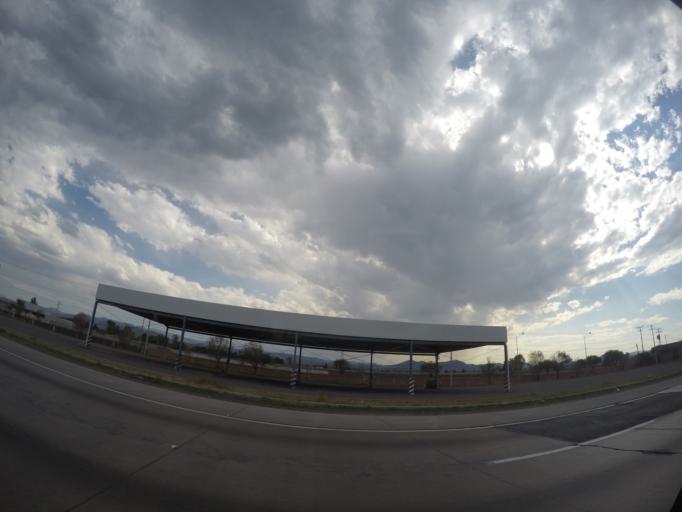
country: MX
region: Queretaro
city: La Estancia
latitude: 20.4152
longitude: -100.0432
